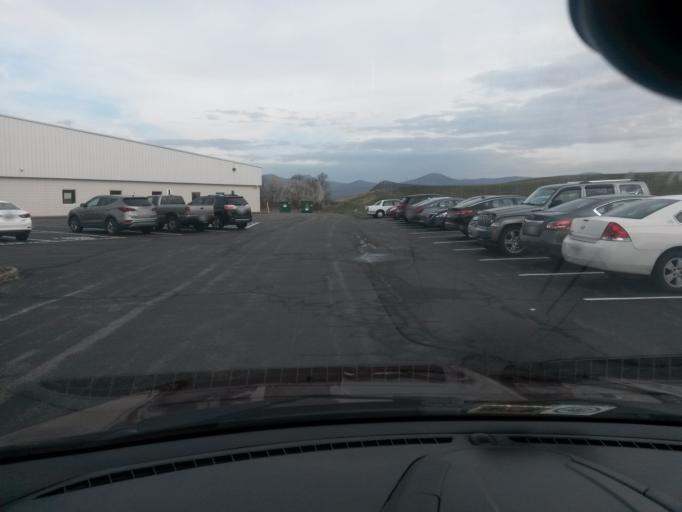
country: US
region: Virginia
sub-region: Roanoke County
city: Hollins
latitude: 37.3117
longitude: -79.9708
